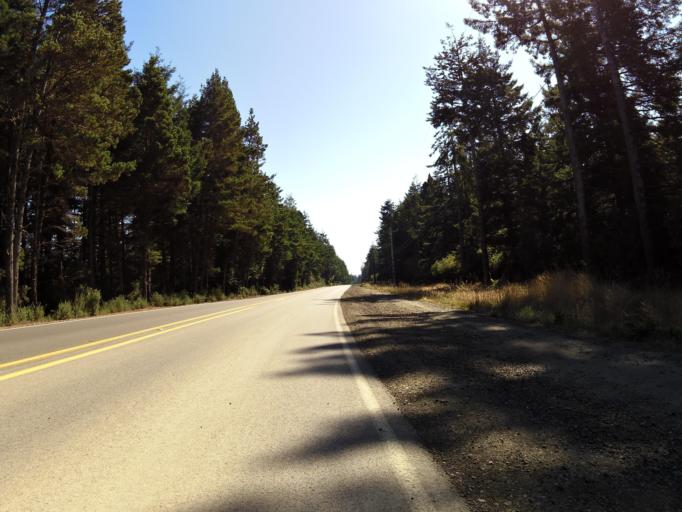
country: US
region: Oregon
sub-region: Coos County
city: Bandon
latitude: 43.2028
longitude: -124.3662
